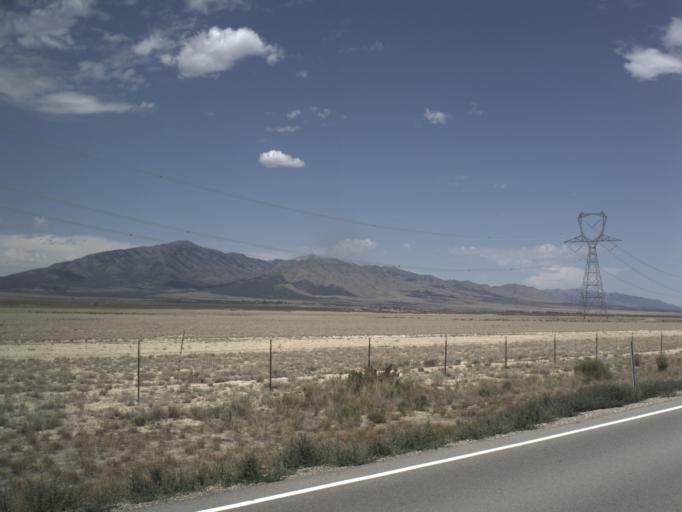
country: US
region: Utah
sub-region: Tooele County
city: Tooele
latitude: 40.2725
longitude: -112.3977
